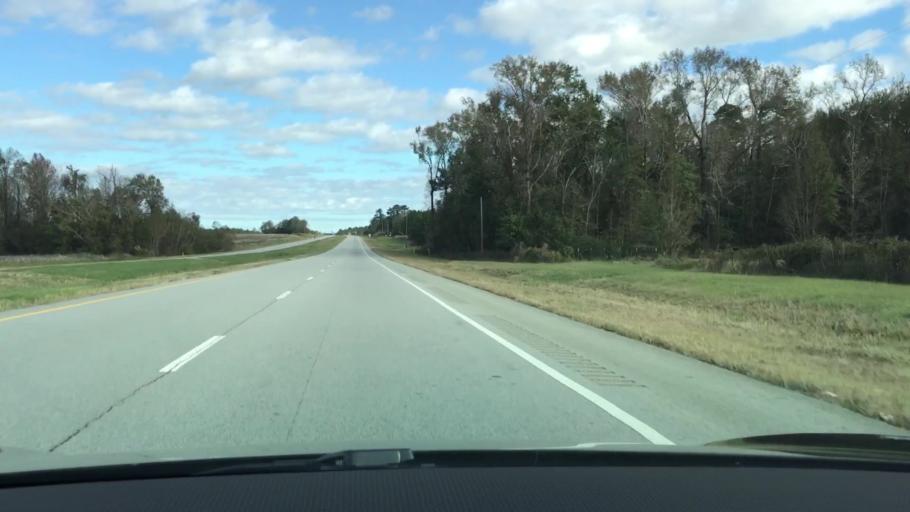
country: US
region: Georgia
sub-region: Jefferson County
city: Wadley
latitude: 32.8340
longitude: -82.4007
